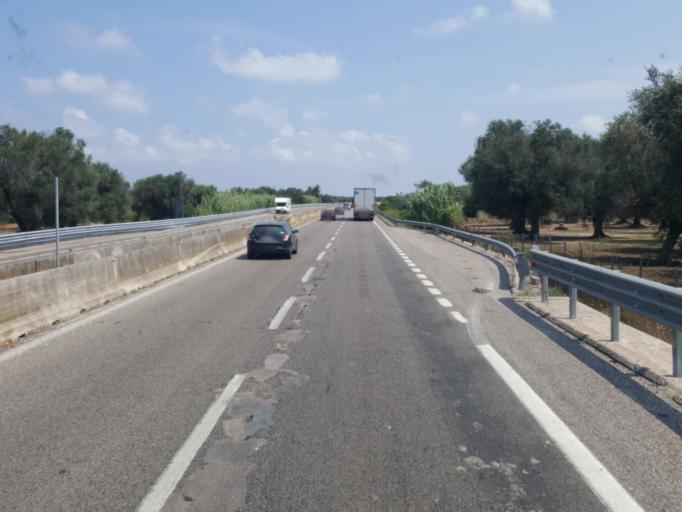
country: IT
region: Apulia
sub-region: Provincia di Brindisi
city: Torchiarolo
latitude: 40.5030
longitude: 18.0271
